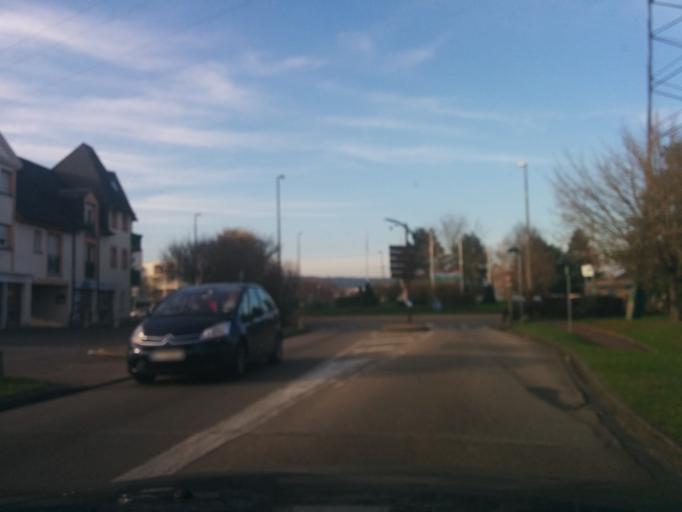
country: FR
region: Haute-Normandie
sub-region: Departement de l'Eure
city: Saint-Marcel
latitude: 49.1017
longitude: 1.4522
